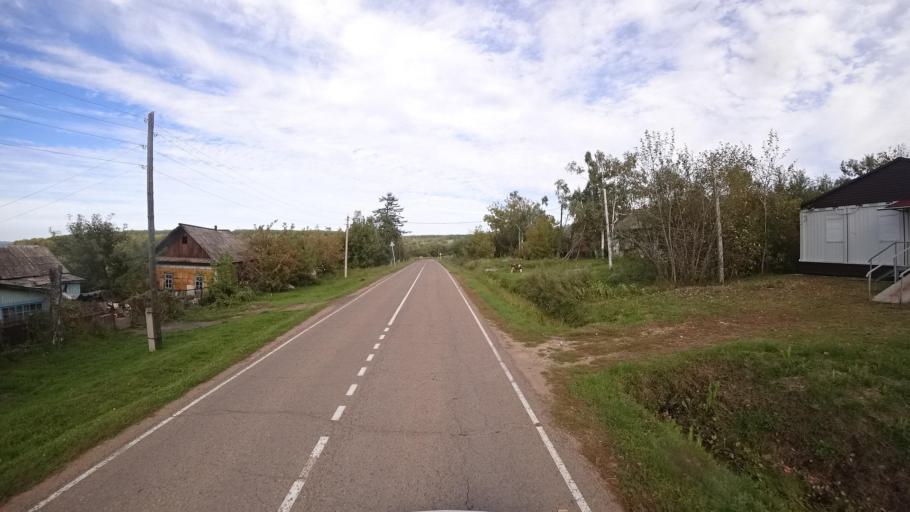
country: RU
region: Primorskiy
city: Dostoyevka
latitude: 44.3285
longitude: 133.4779
